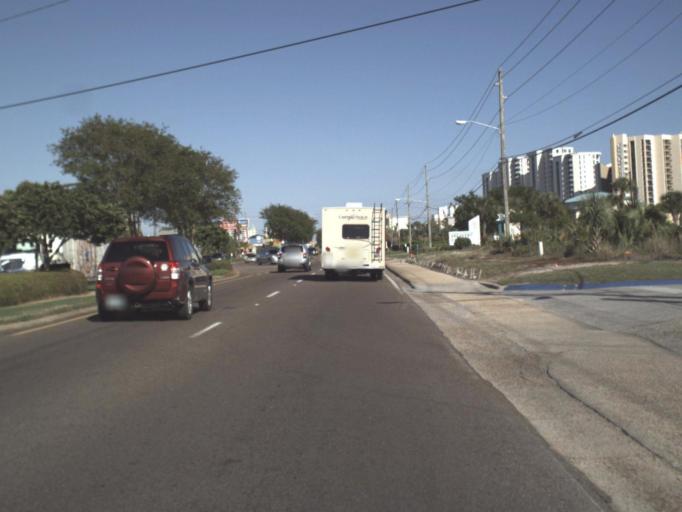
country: US
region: Florida
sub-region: Okaloosa County
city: Destin
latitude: 30.3872
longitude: -86.4727
